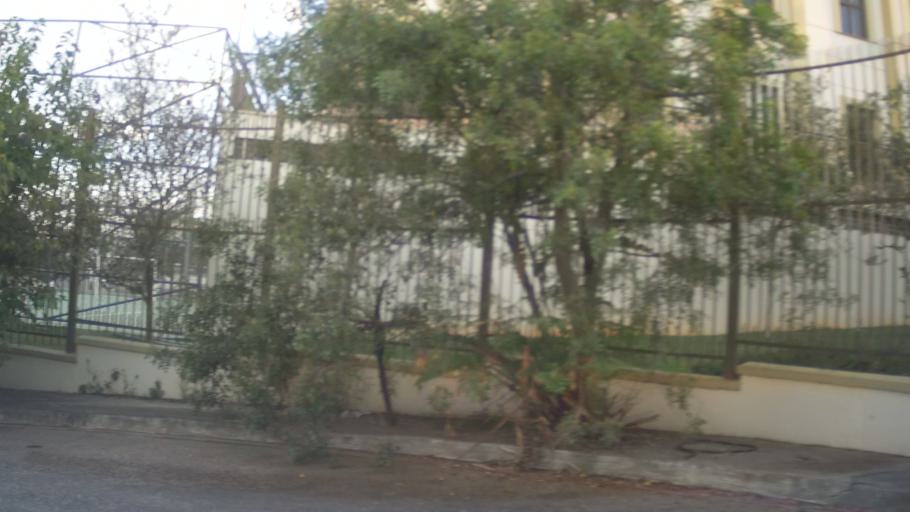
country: BR
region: Sao Paulo
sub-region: Jundiai
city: Jundiai
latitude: -23.1912
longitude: -46.9625
